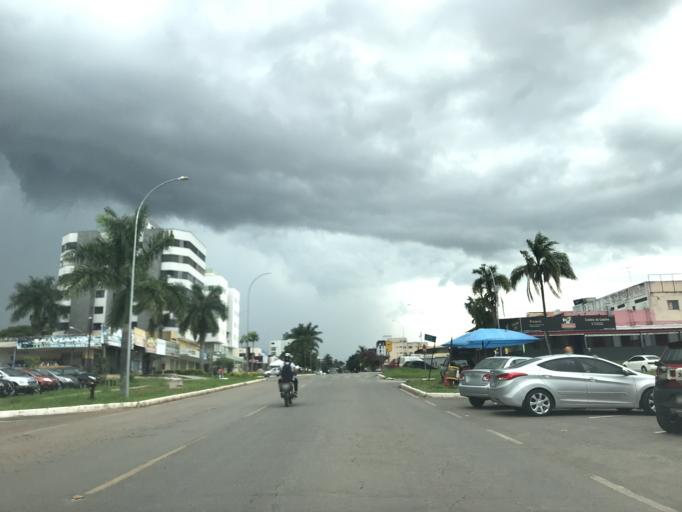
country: BR
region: Federal District
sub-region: Brasilia
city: Brasilia
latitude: -15.6466
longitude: -47.8082
